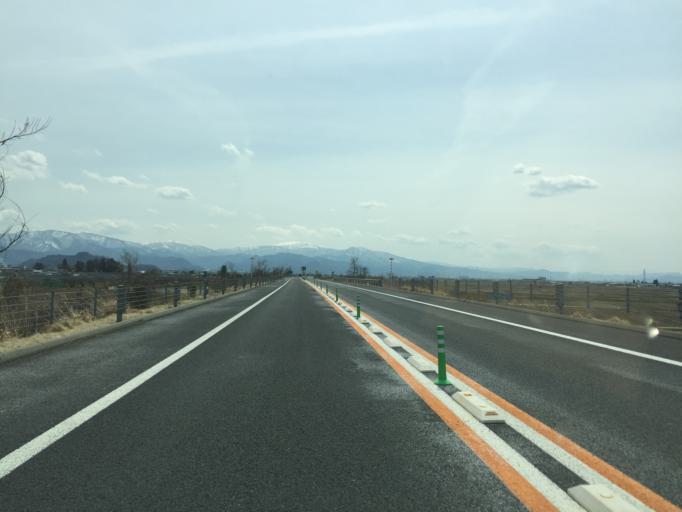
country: JP
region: Yamagata
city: Tendo
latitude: 38.3880
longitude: 140.3438
